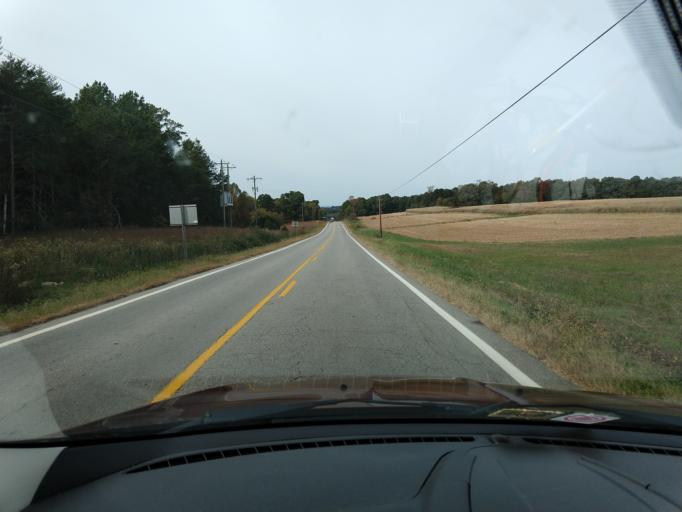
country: US
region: Virginia
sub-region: Pittsylvania County
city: Gretna
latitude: 36.9451
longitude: -79.4702
